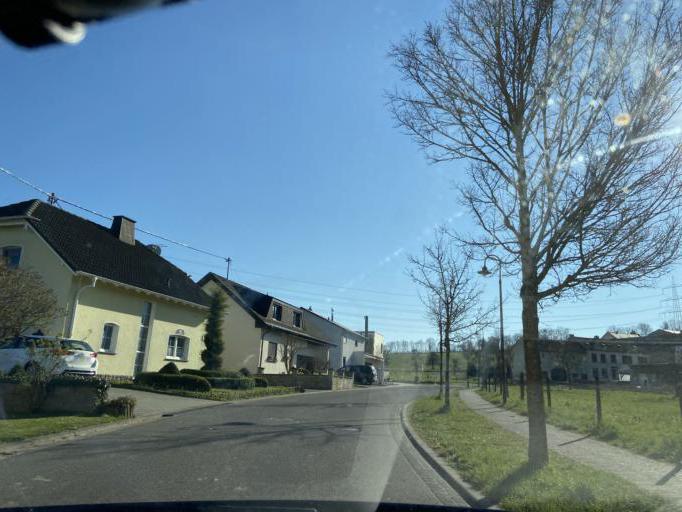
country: DE
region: Rheinland-Pfalz
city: Aach
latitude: 49.8015
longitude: 6.6053
